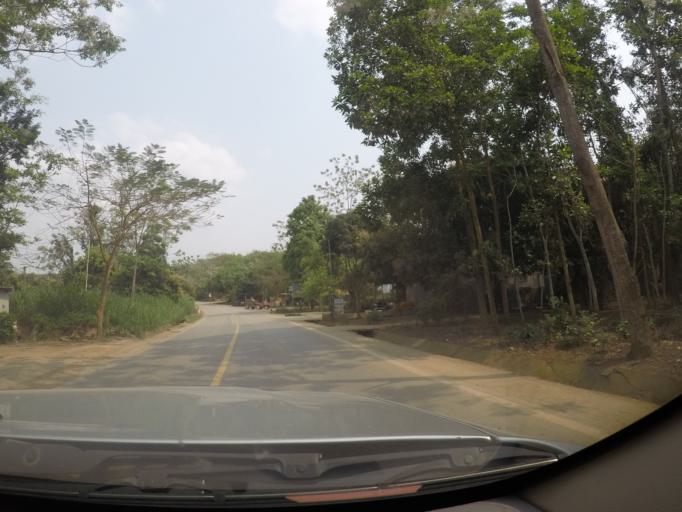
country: VN
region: Thanh Hoa
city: Thi Tran Yen Cat
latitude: 19.4783
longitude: 105.3988
